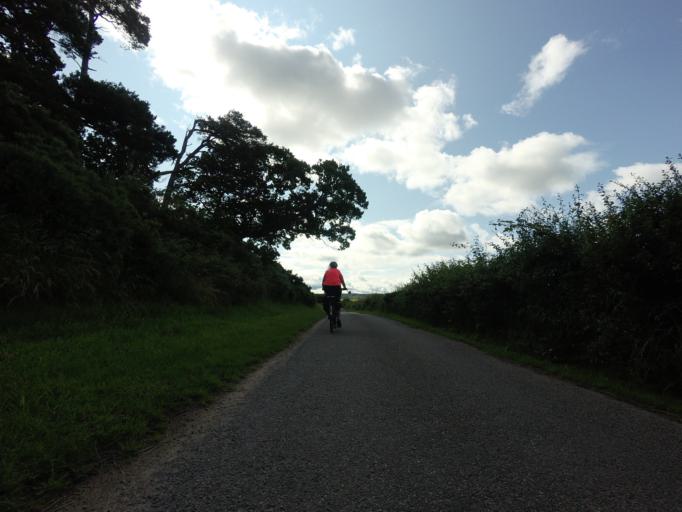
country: GB
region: Scotland
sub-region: Moray
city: Kinloss
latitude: 57.6387
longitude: -3.5209
